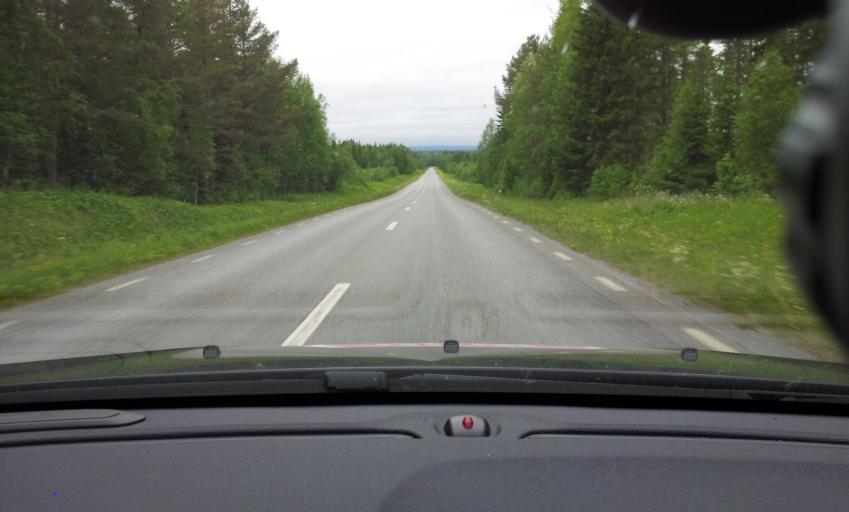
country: SE
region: Jaemtland
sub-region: Krokoms Kommun
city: Krokom
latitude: 63.1330
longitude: 14.2523
